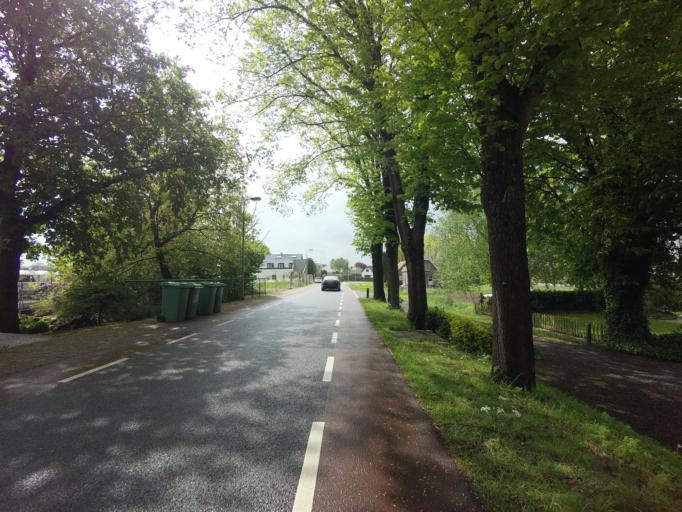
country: NL
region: South Holland
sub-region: Gemeente Ridderkerk
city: Ridderkerk
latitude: 51.8555
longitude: 4.5863
